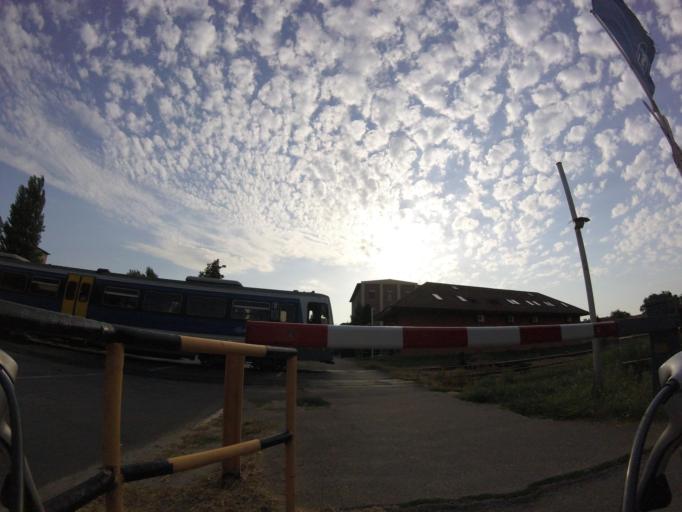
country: HU
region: Bacs-Kiskun
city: Baja
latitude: 46.1851
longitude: 18.9589
